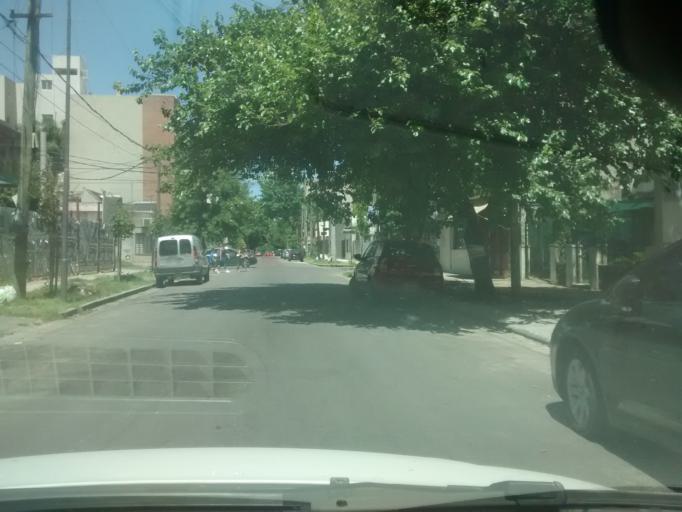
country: AR
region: Buenos Aires
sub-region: Partido de Moron
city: Moron
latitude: -34.6535
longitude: -58.6163
